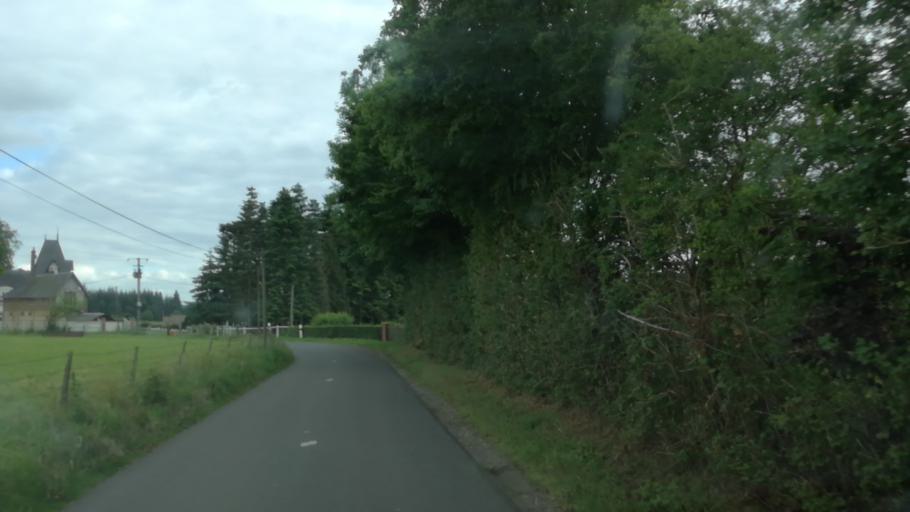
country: FR
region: Haute-Normandie
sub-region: Departement de l'Eure
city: Bourg-Achard
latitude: 49.2939
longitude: 0.8047
